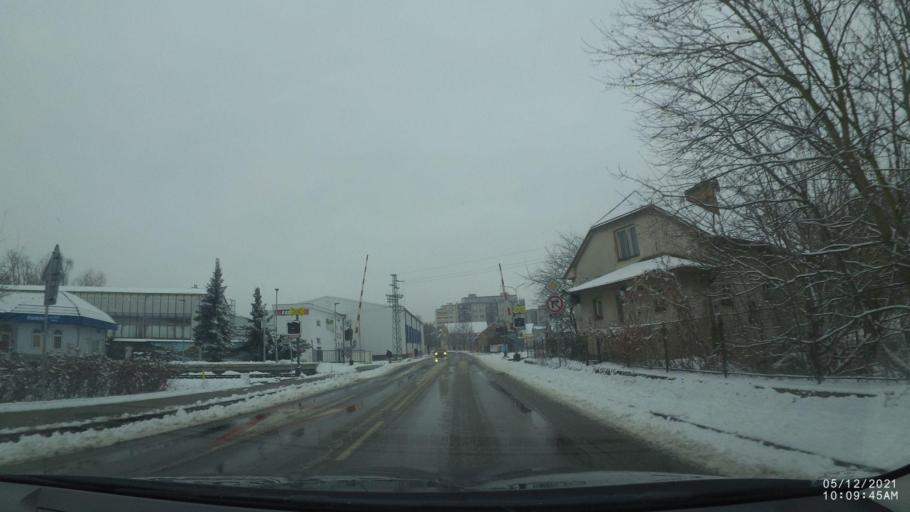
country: CZ
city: Kostelec nad Orlici
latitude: 50.1197
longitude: 16.2050
